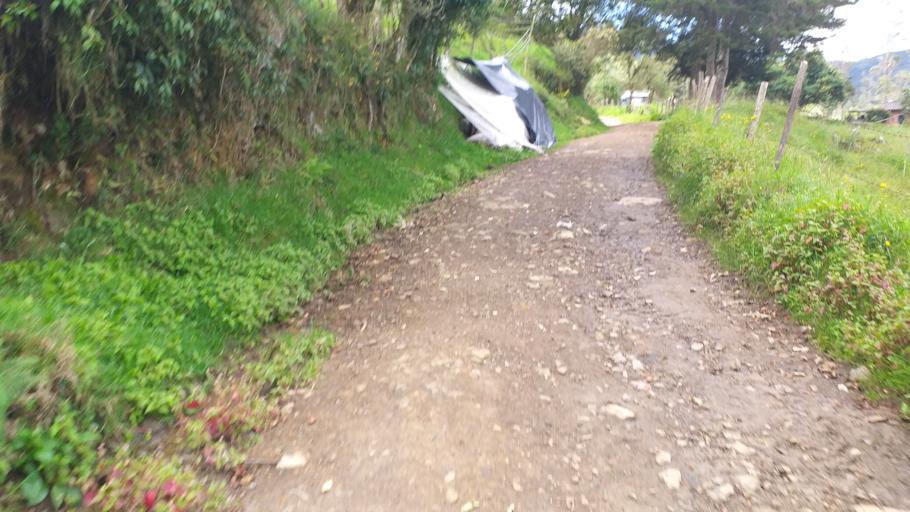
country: CO
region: Cundinamarca
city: Tenza
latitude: 5.1254
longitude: -73.4587
